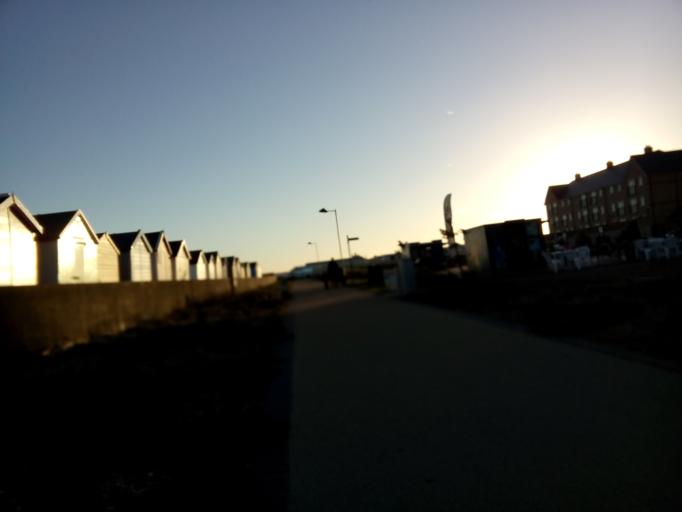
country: GB
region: England
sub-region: Suffolk
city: Felixstowe
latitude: 51.9475
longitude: 1.3345
